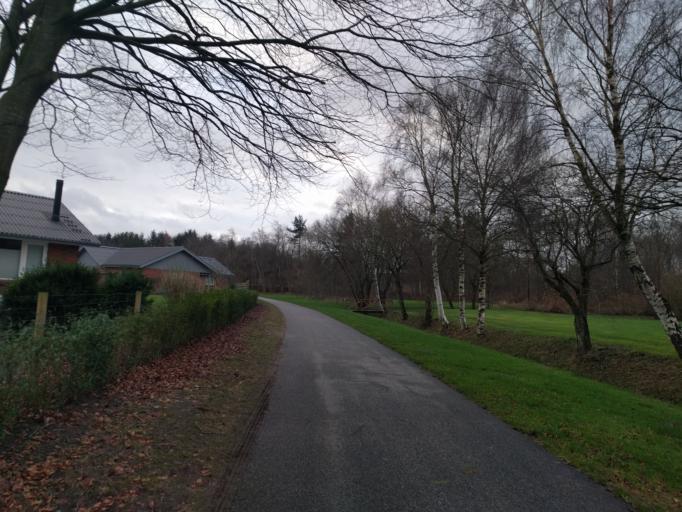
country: DK
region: Central Jutland
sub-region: Viborg Kommune
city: Viborg
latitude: 56.4561
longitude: 9.3756
